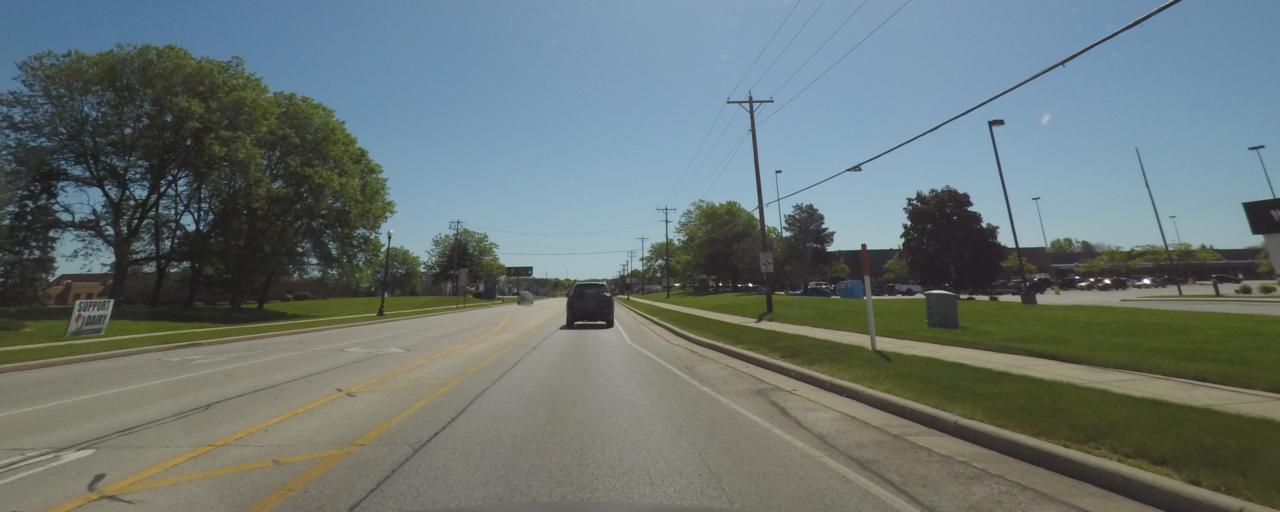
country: US
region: Wisconsin
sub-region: Sheboygan County
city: Plymouth
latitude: 43.7469
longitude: -87.9510
